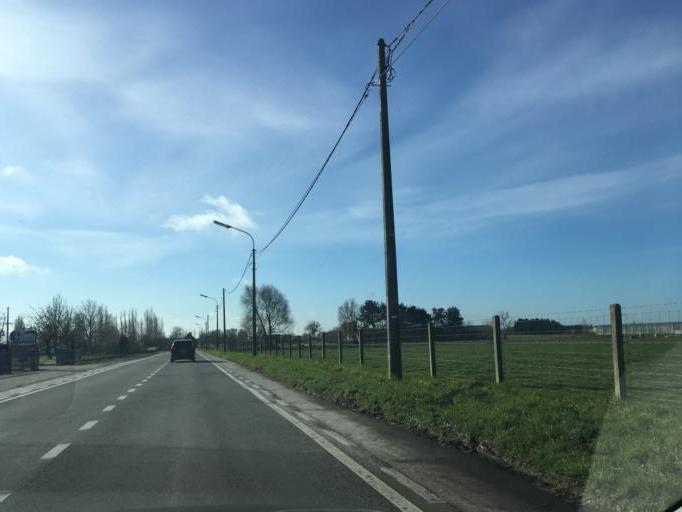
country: BE
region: Flanders
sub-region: Provincie West-Vlaanderen
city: Ledegem
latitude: 50.8625
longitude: 3.1529
